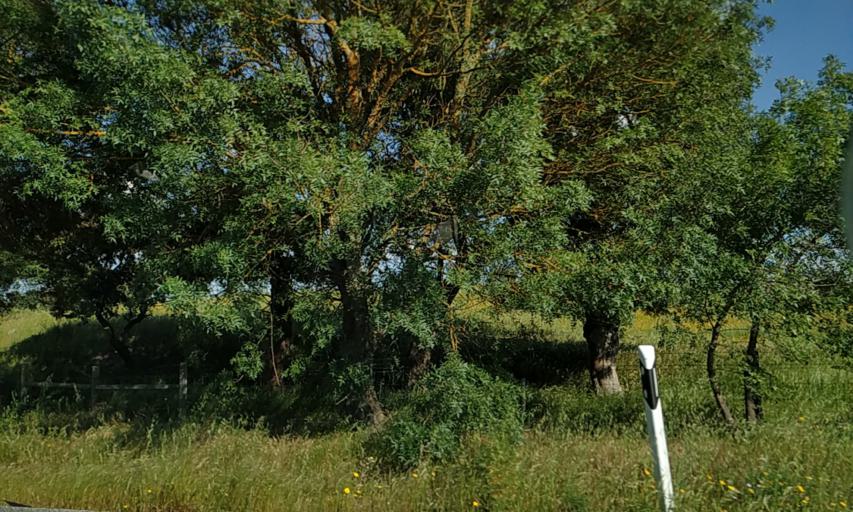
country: PT
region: Evora
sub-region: Estremoz
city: Estremoz
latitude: 38.9870
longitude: -7.4774
